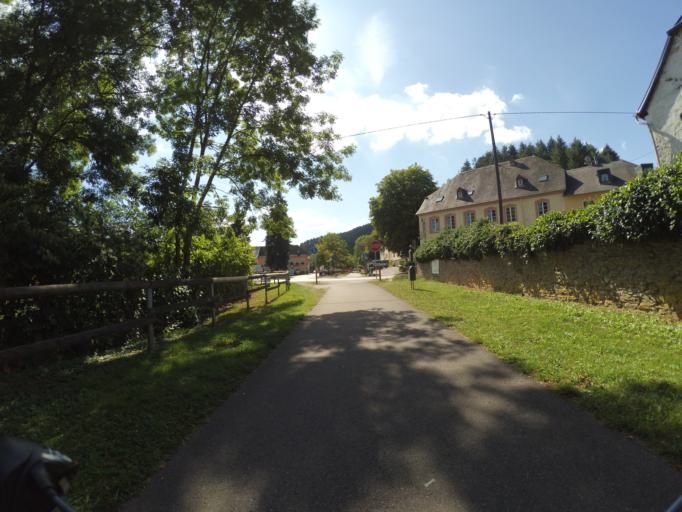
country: DE
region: Rheinland-Pfalz
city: Kasel
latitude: 49.7629
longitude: 6.7262
